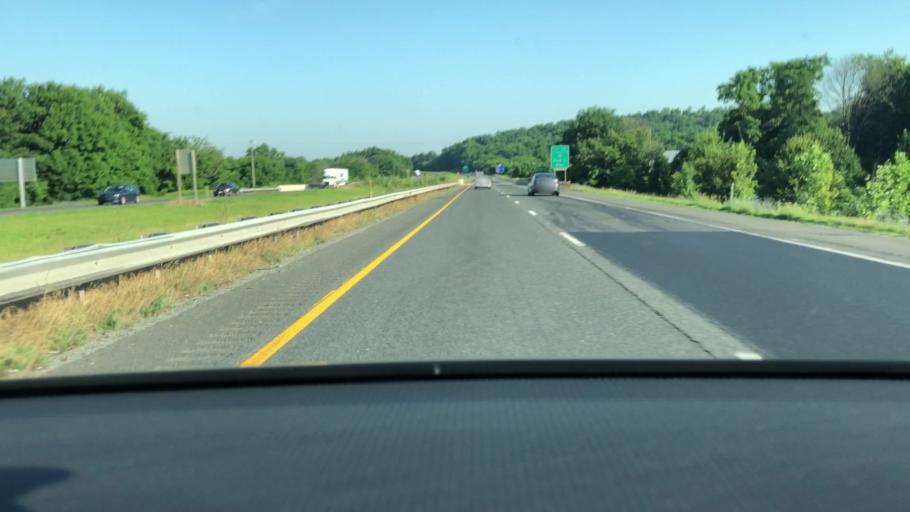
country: US
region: Maryland
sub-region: Washington County
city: Robinwood
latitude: 39.5775
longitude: -77.6276
